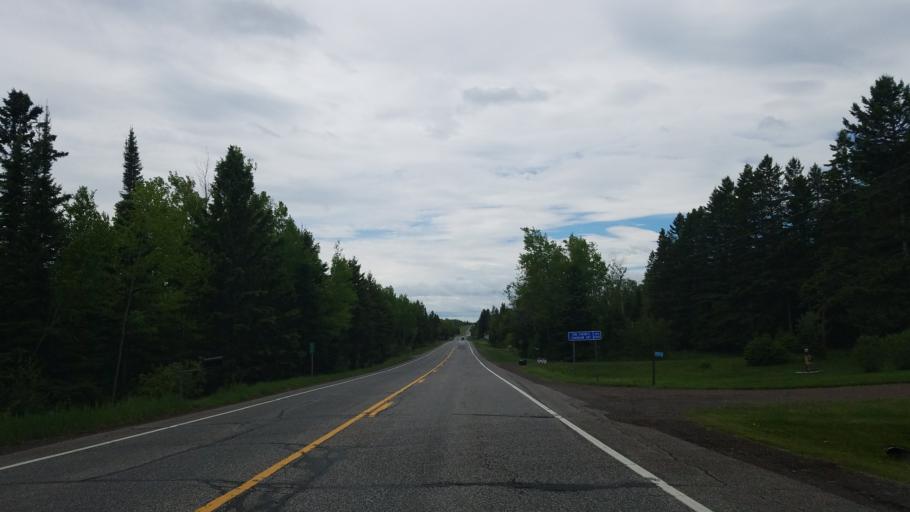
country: US
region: Minnesota
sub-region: Lake County
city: Two Harbors
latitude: 47.0436
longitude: -91.6367
